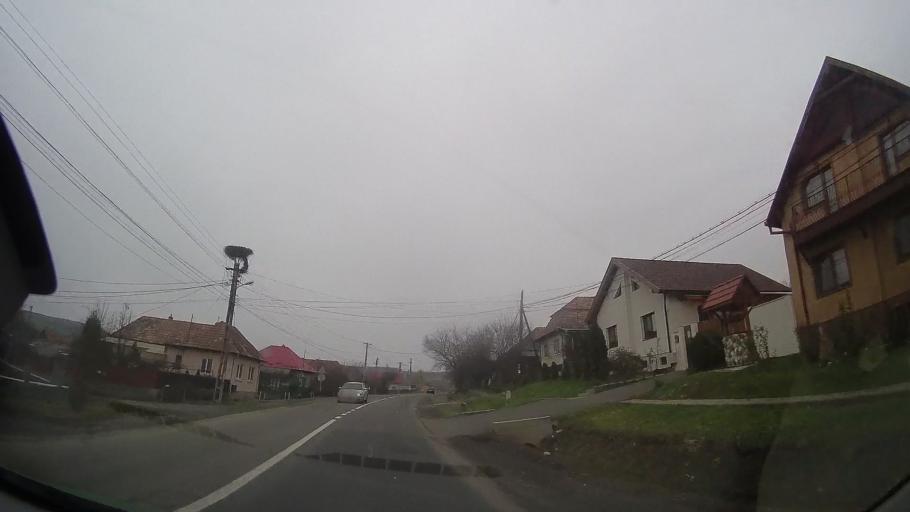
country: RO
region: Mures
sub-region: Comuna Ceausu de Campie
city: Ceausu de Campie
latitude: 46.6451
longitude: 24.4988
